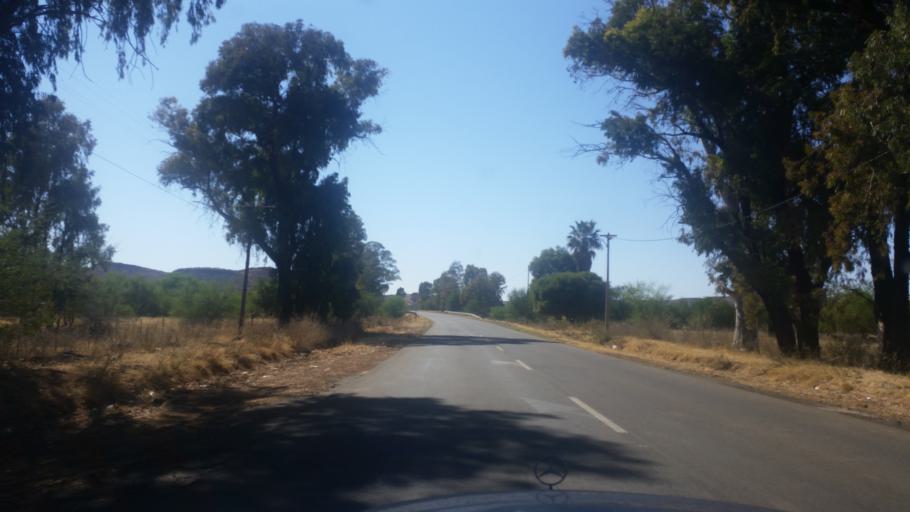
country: ZA
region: Orange Free State
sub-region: Xhariep District Municipality
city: Trompsburg
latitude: -30.4967
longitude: 25.9840
